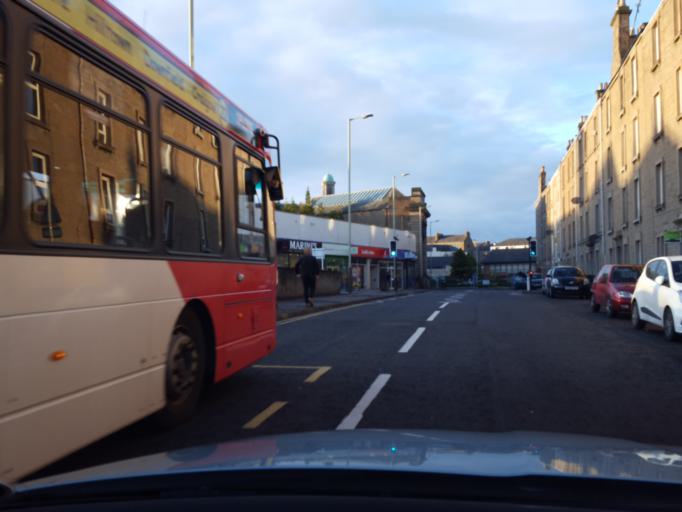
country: GB
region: Scotland
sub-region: Dundee City
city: Dundee
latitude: 56.4741
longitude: -2.9797
